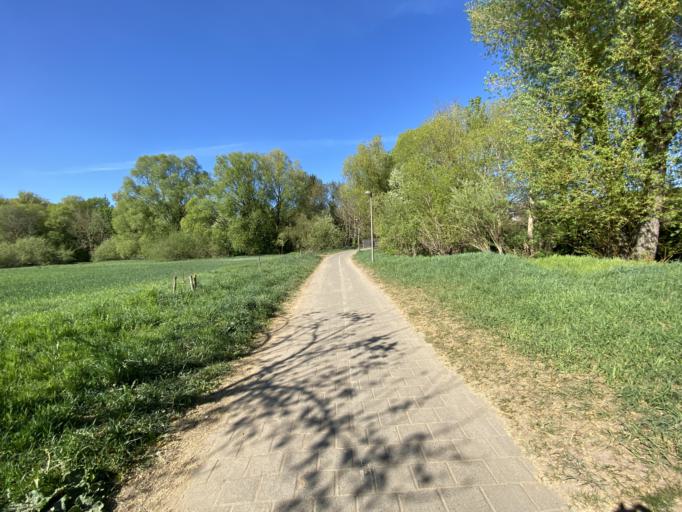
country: DE
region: Bavaria
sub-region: Regierungsbezirk Mittelfranken
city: Buckenhof
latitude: 49.5970
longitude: 11.0423
